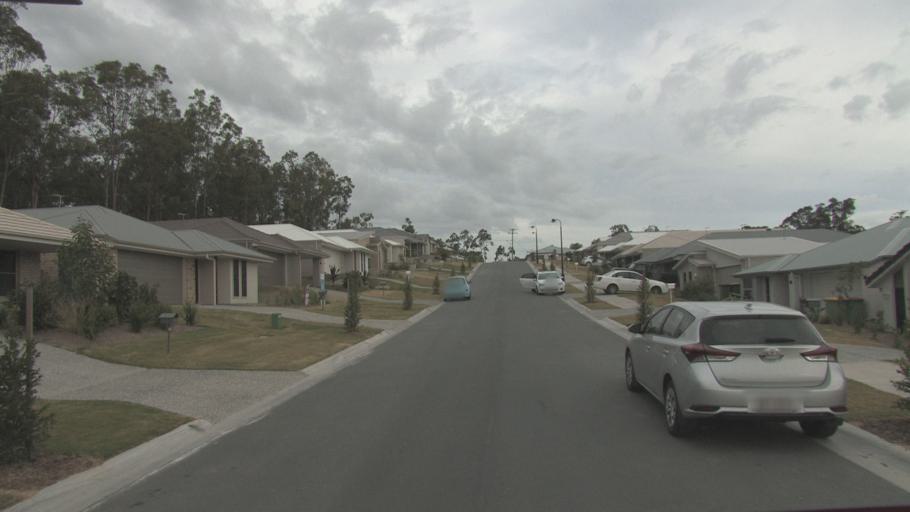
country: AU
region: Queensland
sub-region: Logan
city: Windaroo
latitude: -27.7242
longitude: 153.1646
